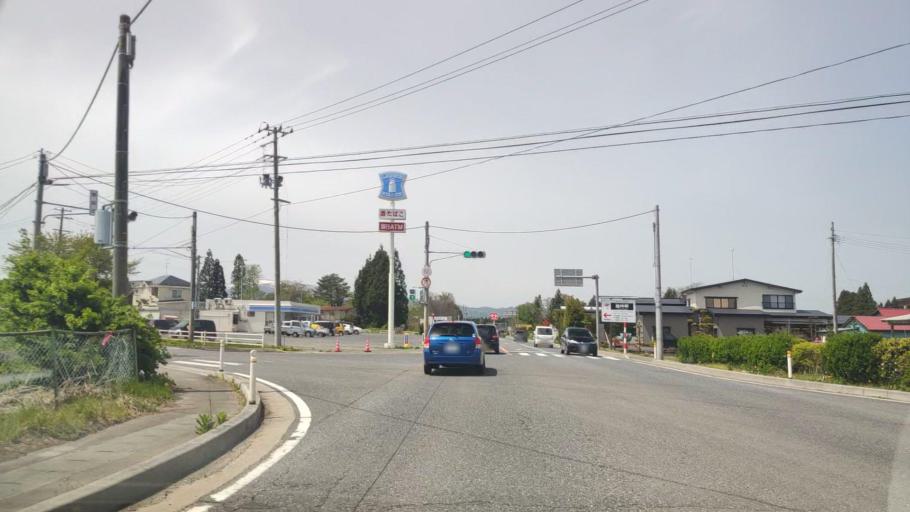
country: JP
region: Aomori
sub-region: Misawa Shi
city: Inuotose
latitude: 40.6727
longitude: 141.1813
